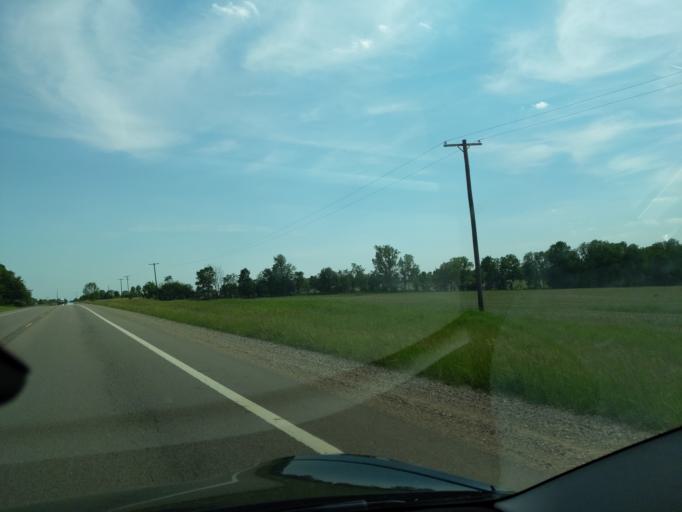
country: US
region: Michigan
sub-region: Barry County
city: Nashville
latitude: 42.6343
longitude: -85.0949
